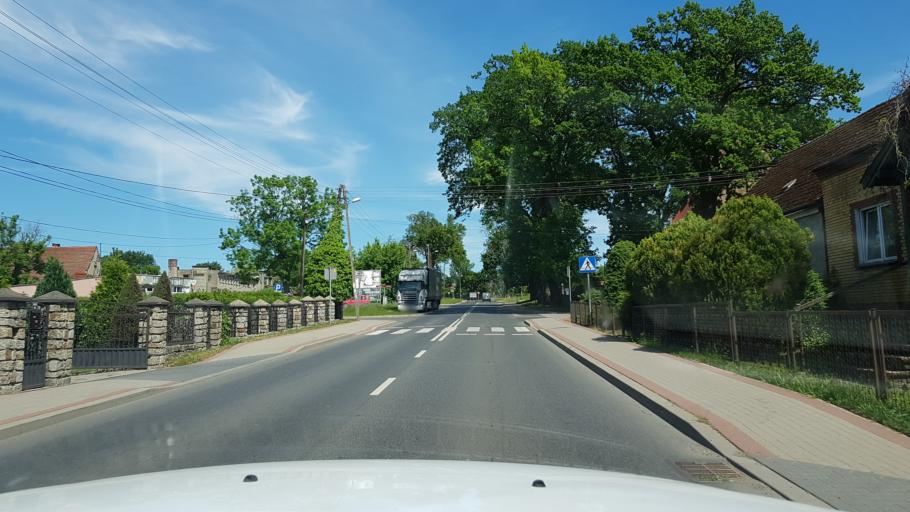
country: PL
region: West Pomeranian Voivodeship
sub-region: Powiat gryfinski
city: Chojna
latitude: 52.9631
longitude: 14.4506
